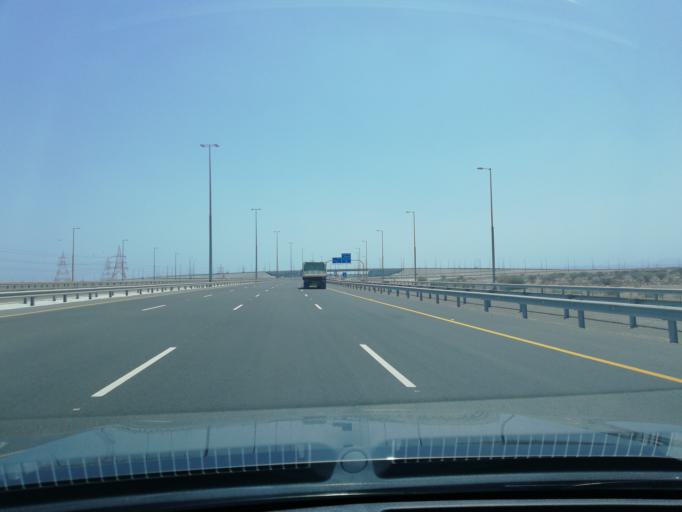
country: OM
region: Al Batinah
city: Barka'
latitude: 23.6330
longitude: 57.8656
